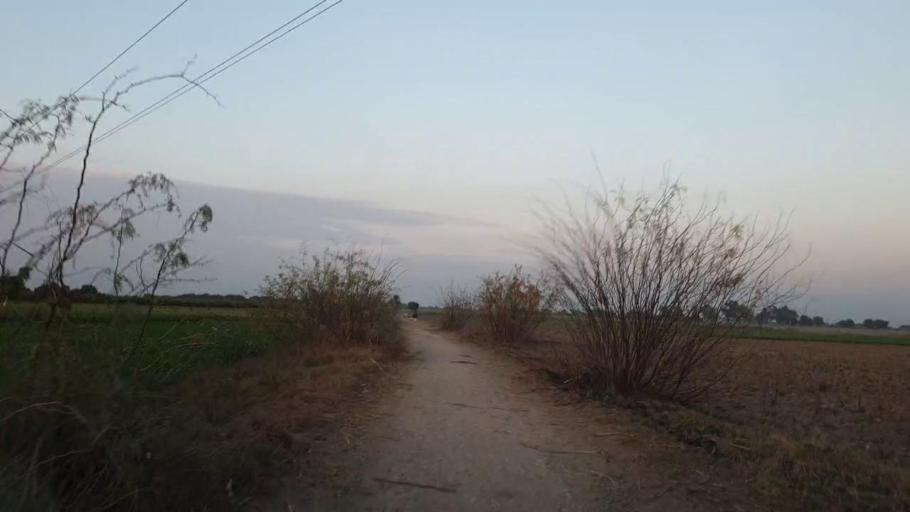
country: PK
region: Sindh
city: Tando Jam
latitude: 25.5078
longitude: 68.5819
